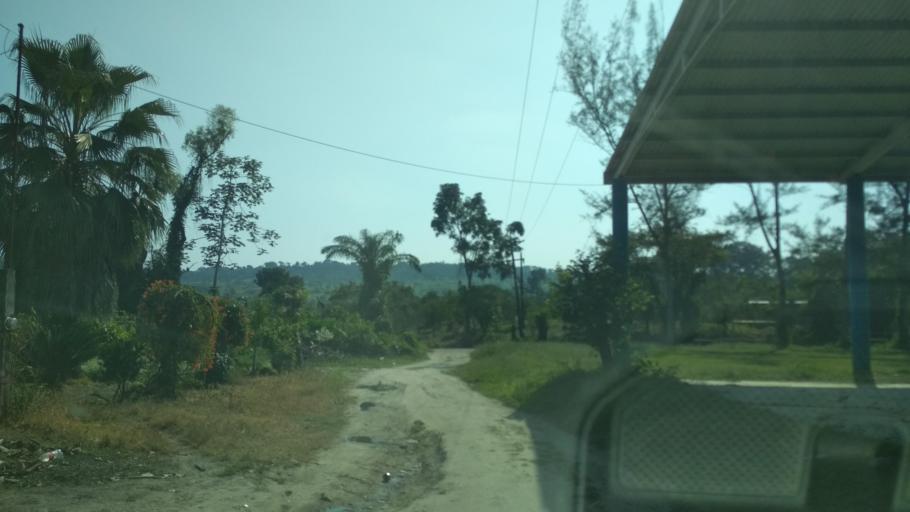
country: MX
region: Puebla
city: San Jose Acateno
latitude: 20.1793
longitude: -97.2587
